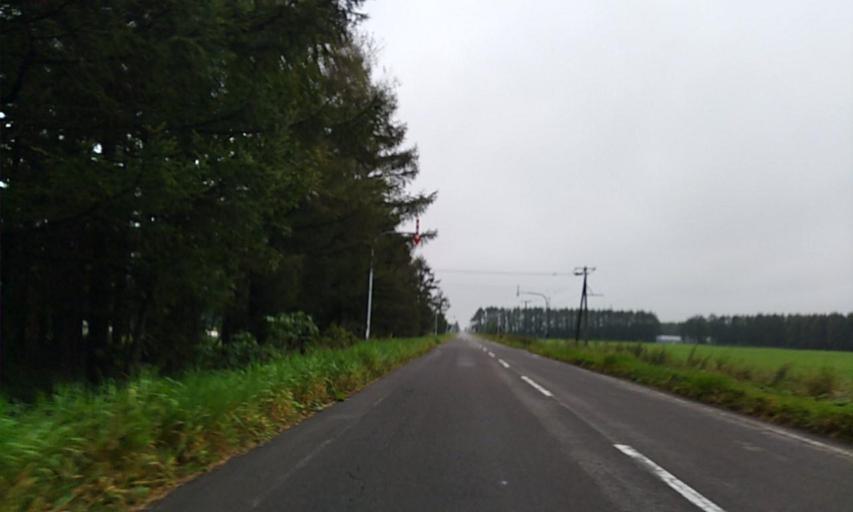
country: JP
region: Hokkaido
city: Shibetsu
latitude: 43.5155
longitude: 144.6777
